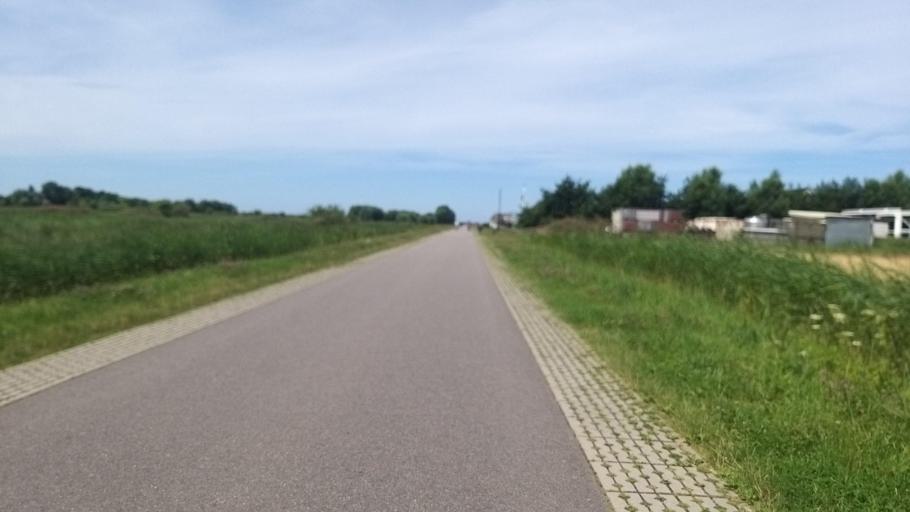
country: NL
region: North Holland
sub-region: Gemeente Texel
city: Den Burg
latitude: 53.1154
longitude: 4.8536
